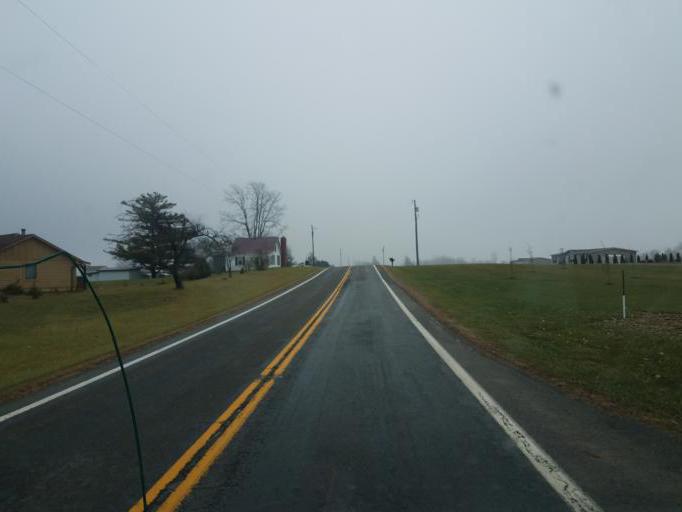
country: US
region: Ohio
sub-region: Champaign County
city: North Lewisburg
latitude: 40.2673
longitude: -83.5917
